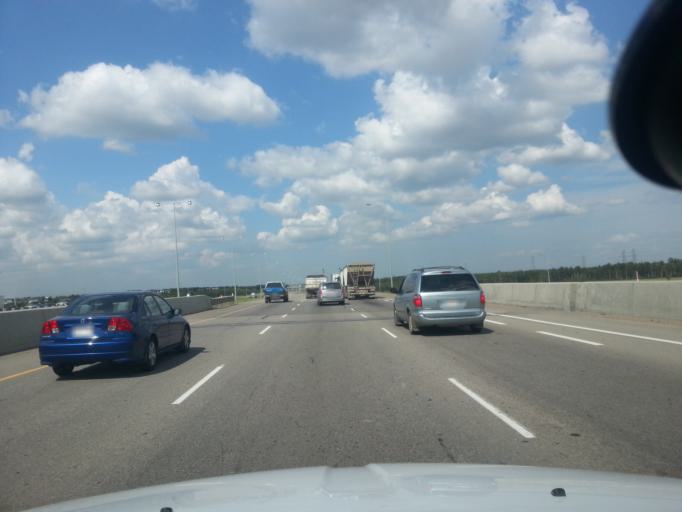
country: CA
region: Alberta
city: St. Albert
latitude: 53.5412
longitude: -113.6588
